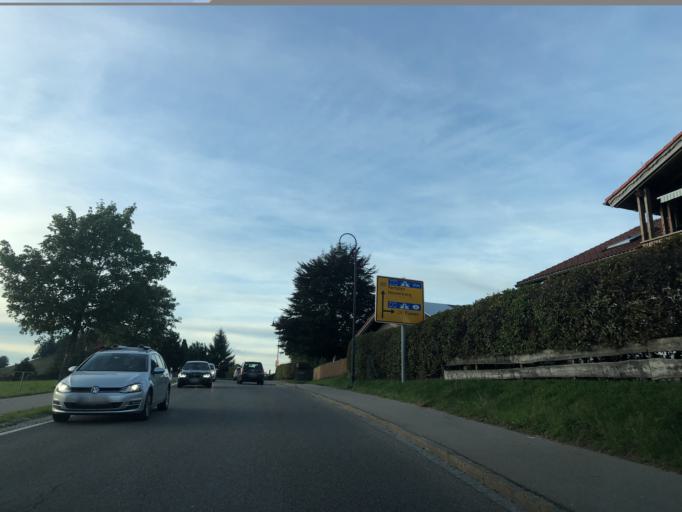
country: DE
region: Bavaria
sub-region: Swabia
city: Pfronten
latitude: 47.5926
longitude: 10.5565
